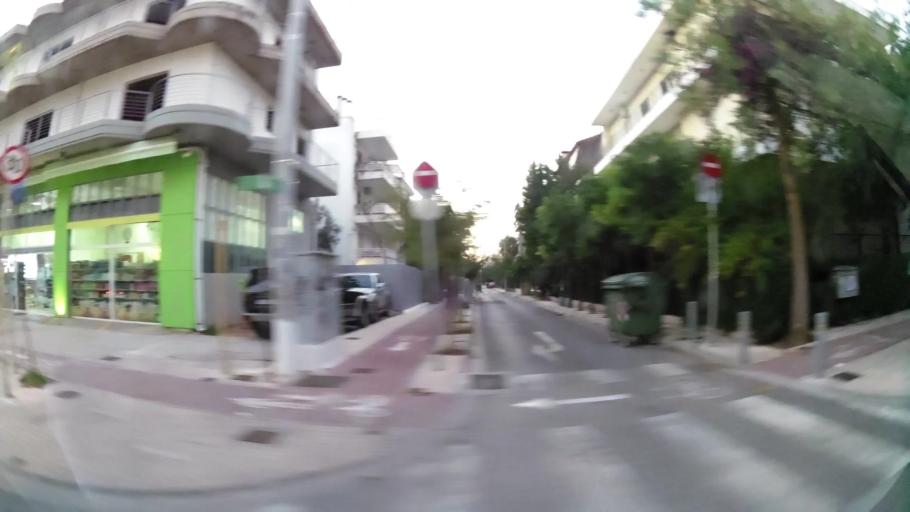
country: GR
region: Attica
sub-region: Nomarchia Athinas
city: Agia Paraskevi
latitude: 38.0201
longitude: 23.8353
